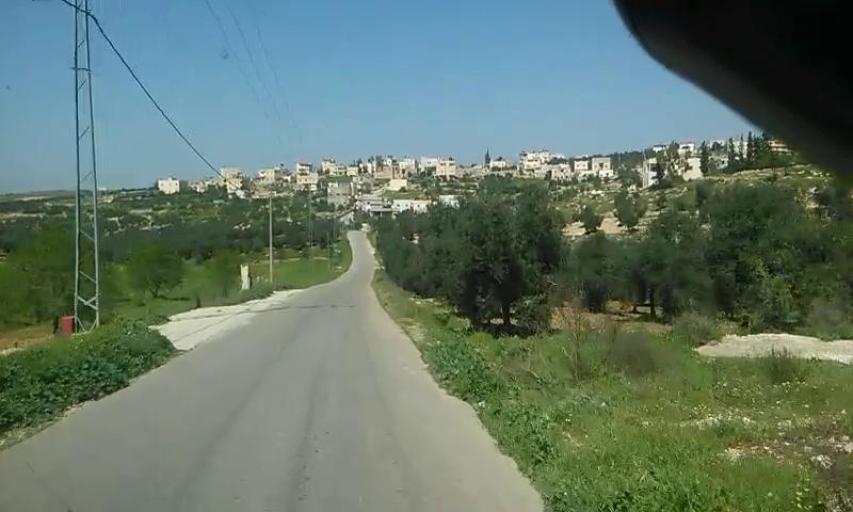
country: PS
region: West Bank
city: Al Majd
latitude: 31.4881
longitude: 34.9437
